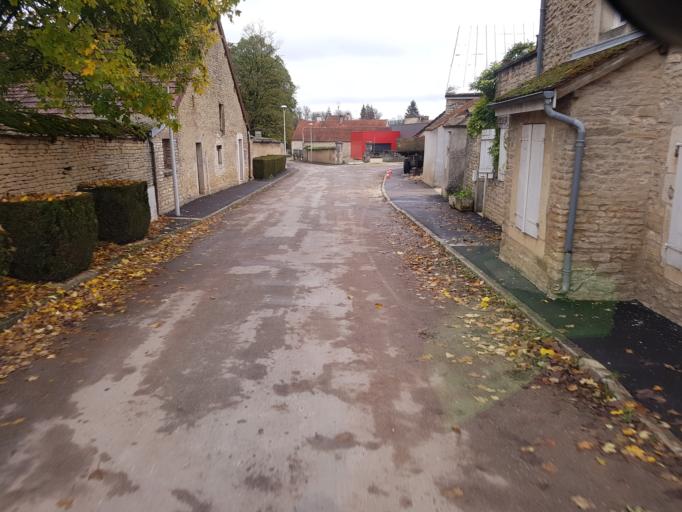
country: FR
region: Bourgogne
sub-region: Departement de la Cote-d'Or
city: Is-sur-Tille
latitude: 47.5335
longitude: 4.9831
